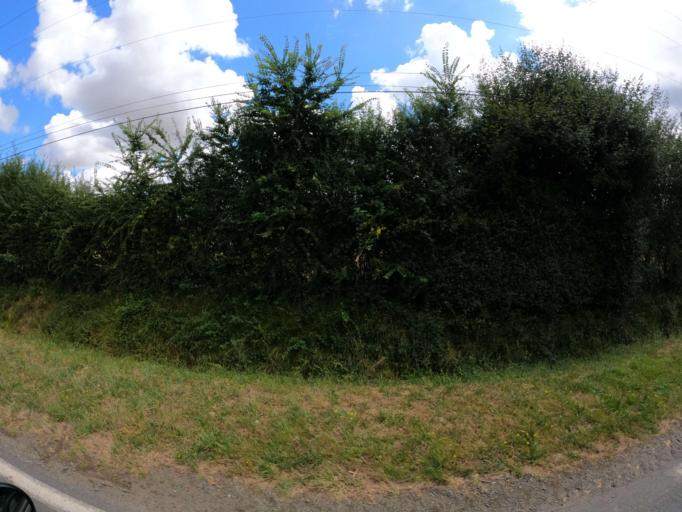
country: FR
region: Pays de la Loire
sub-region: Departement de la Sarthe
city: Juigne-sur-Sarthe
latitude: 47.8830
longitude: -0.2980
